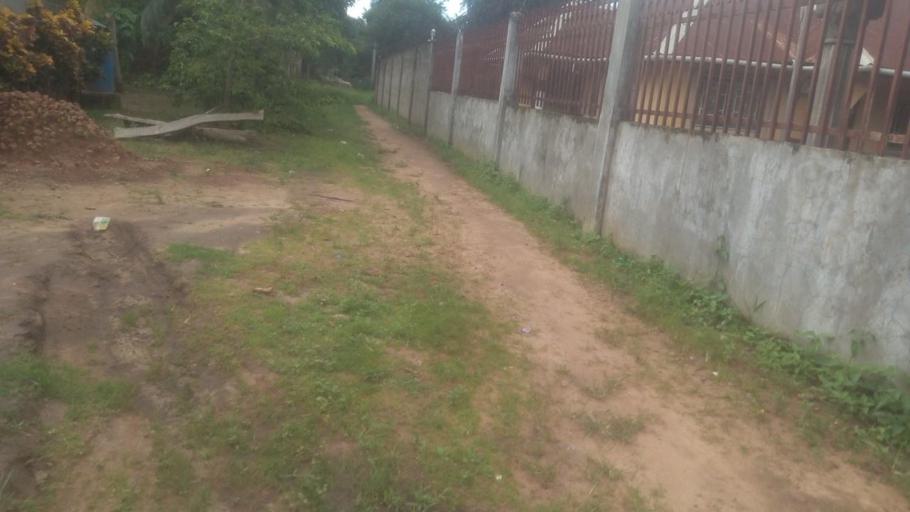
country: SL
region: Northern Province
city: Masoyila
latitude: 8.5617
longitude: -13.1651
